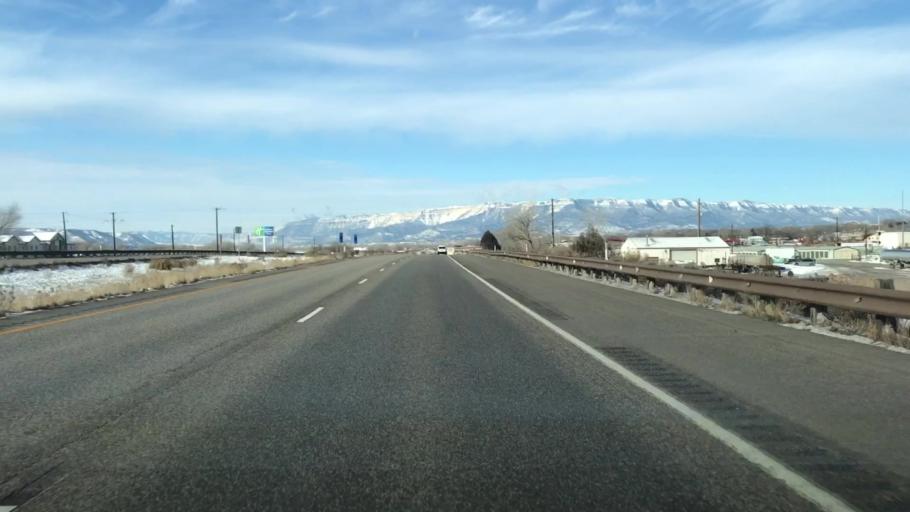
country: US
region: Colorado
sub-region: Garfield County
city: Silt
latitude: 39.5441
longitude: -107.6441
